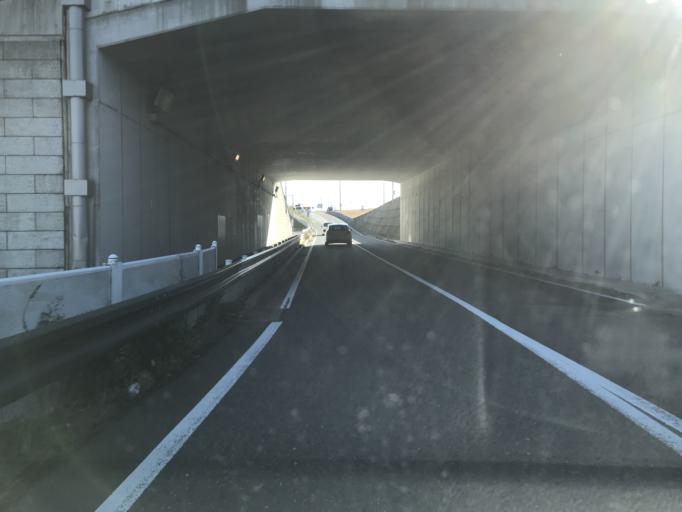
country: JP
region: Aichi
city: Kanie
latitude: 35.1243
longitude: 136.8388
